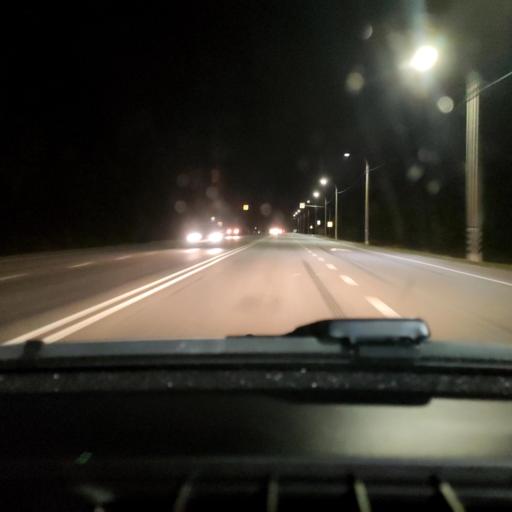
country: RU
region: Voronezj
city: Anna
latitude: 51.5077
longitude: 40.2713
